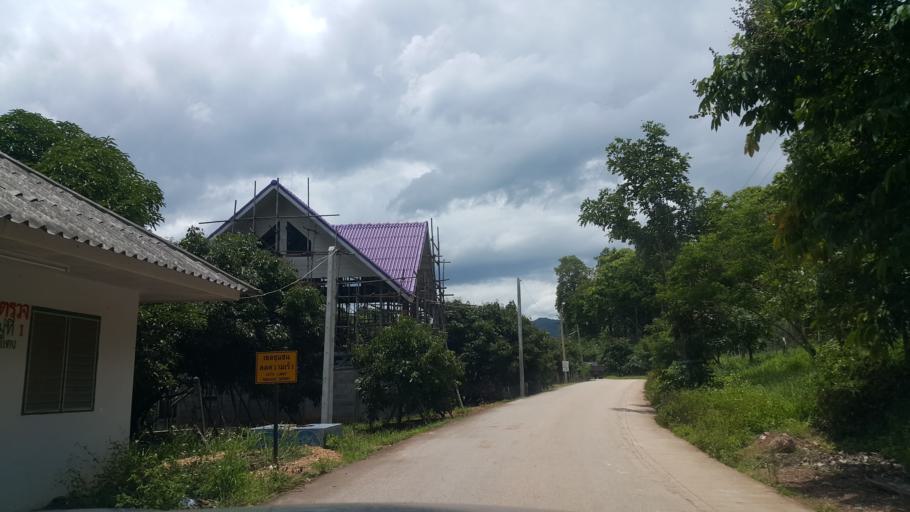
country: TH
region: Chiang Mai
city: Mae Taeng
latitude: 19.2088
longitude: 99.0066
